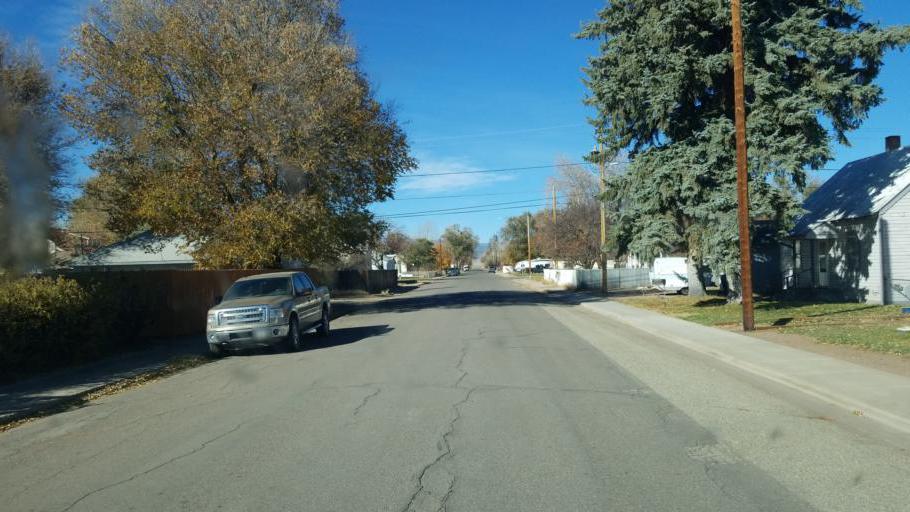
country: US
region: Colorado
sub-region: Rio Grande County
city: Monte Vista
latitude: 37.5780
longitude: -106.1511
